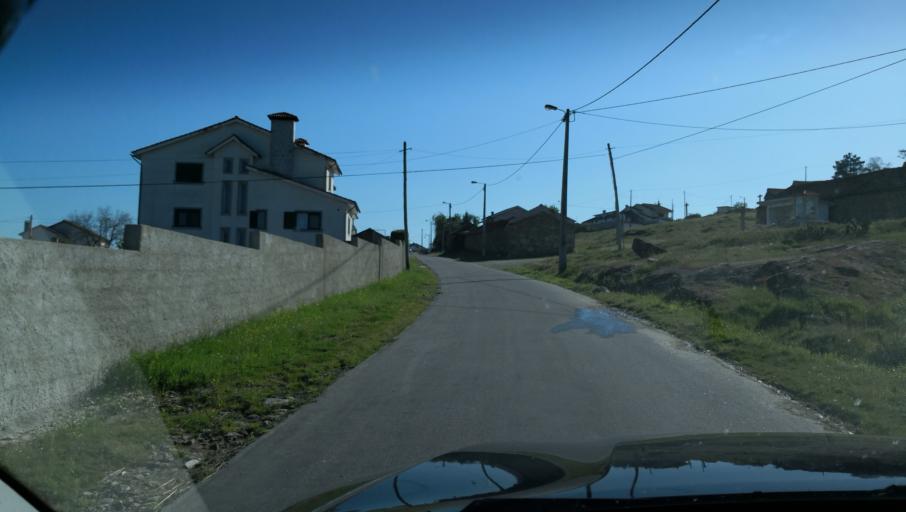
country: PT
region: Vila Real
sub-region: Sabrosa
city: Sabrosa
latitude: 41.2977
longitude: -7.6481
